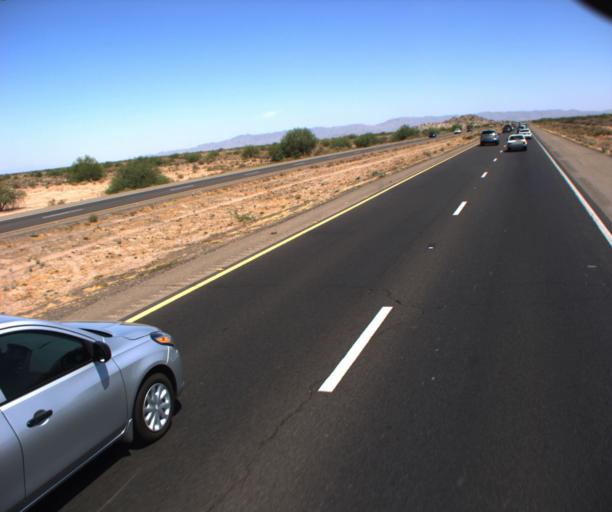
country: US
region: Arizona
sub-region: Pinal County
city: Maricopa
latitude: 33.1534
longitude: -112.0073
